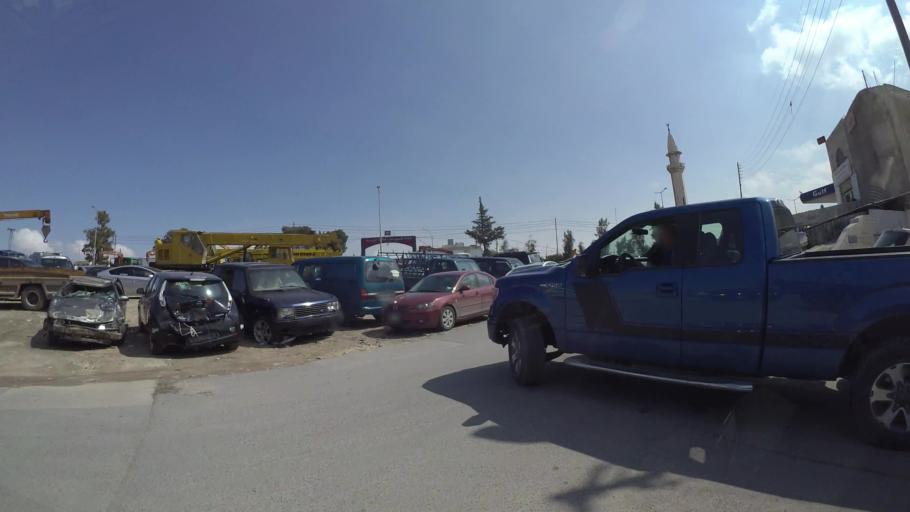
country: JO
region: Zarqa
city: Russeifa
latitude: 31.9927
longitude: 36.0028
